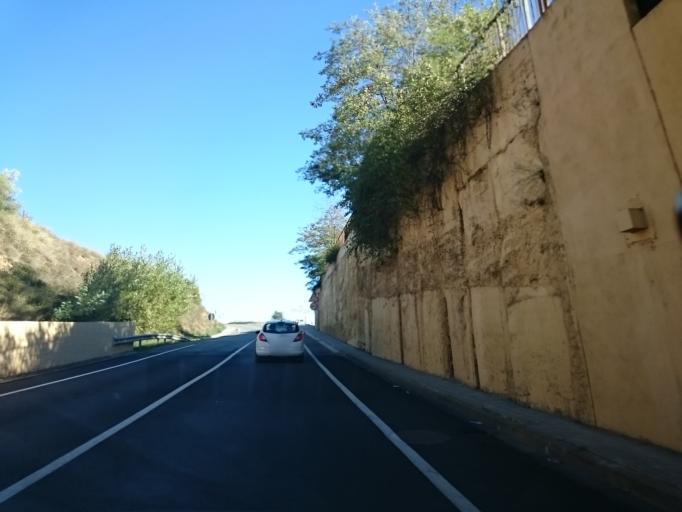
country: ES
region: Catalonia
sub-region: Provincia de Barcelona
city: Piera
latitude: 41.5202
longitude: 1.7584
